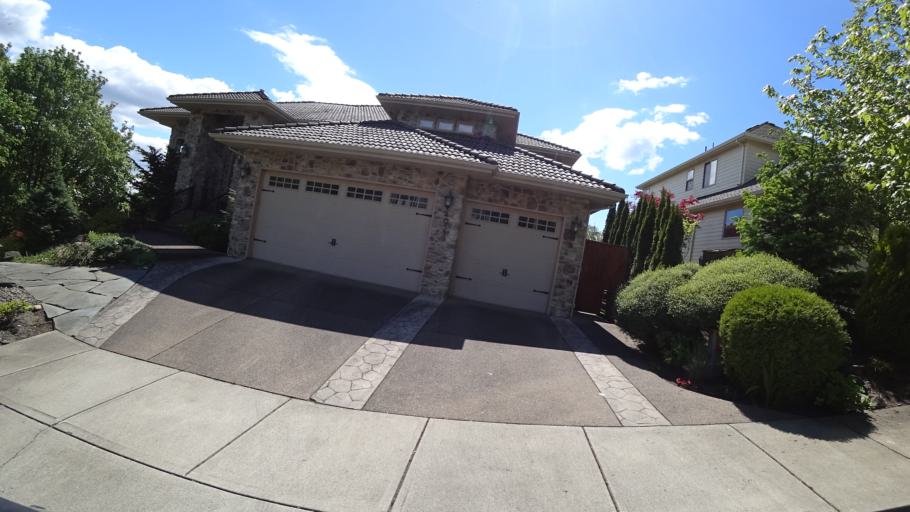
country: US
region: Oregon
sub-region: Washington County
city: West Haven
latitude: 45.5505
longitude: -122.7832
